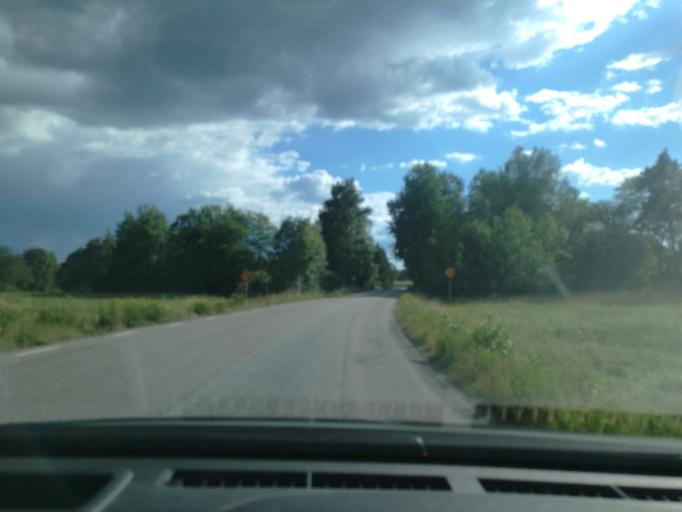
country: SE
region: Soedermanland
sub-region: Eskilstuna Kommun
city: Arla
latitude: 59.4086
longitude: 16.6908
